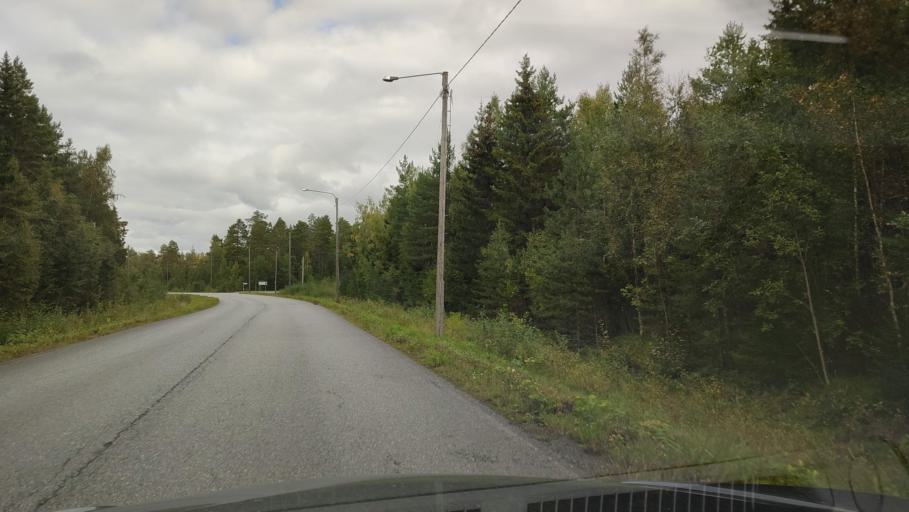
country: FI
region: Ostrobothnia
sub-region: Sydosterbotten
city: Kristinestad
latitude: 62.2613
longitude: 21.3485
